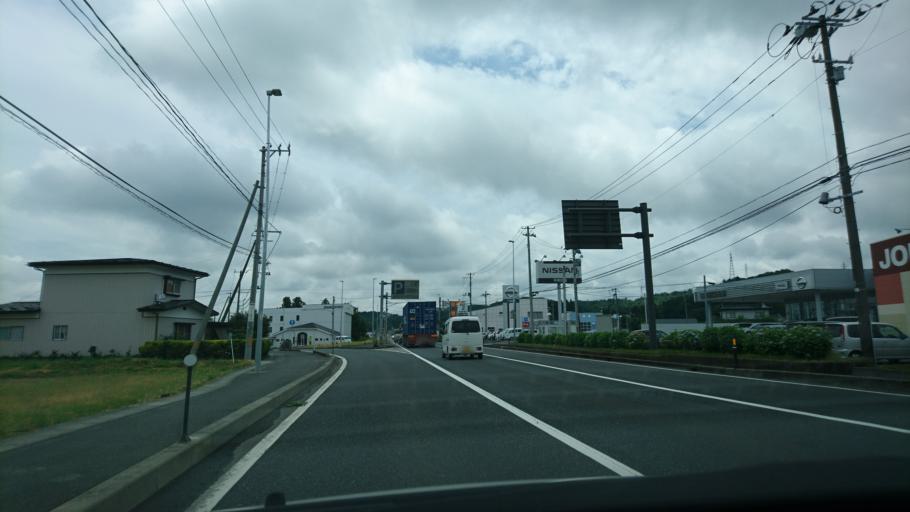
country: JP
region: Iwate
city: Ichinoseki
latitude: 38.9706
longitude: 141.1187
